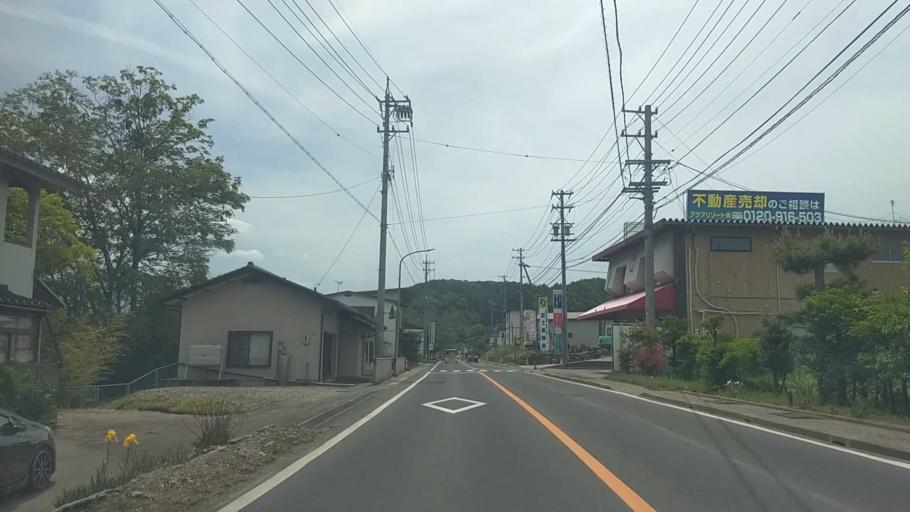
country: JP
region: Nagano
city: Saku
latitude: 36.1819
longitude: 138.4817
